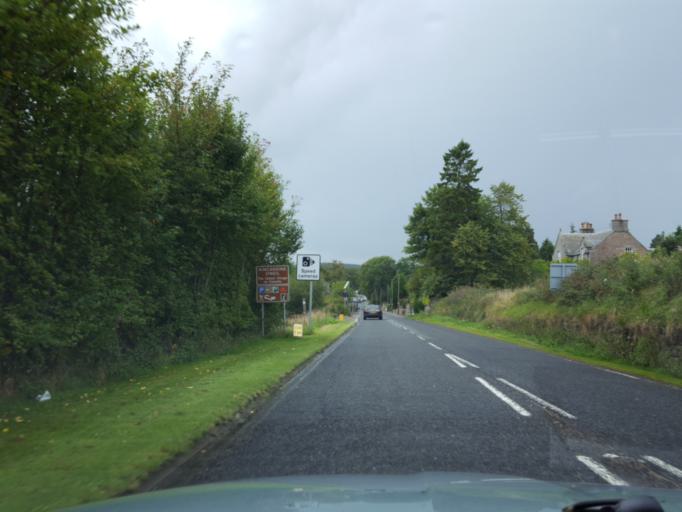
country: GB
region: Scotland
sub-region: Aberdeenshire
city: Torphins
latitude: 57.0839
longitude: -2.6677
